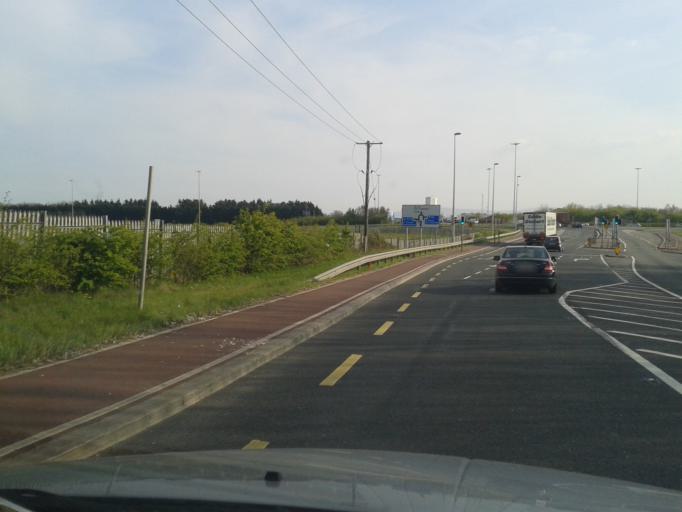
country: IE
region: Leinster
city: Ballymun
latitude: 53.4120
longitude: -6.2652
